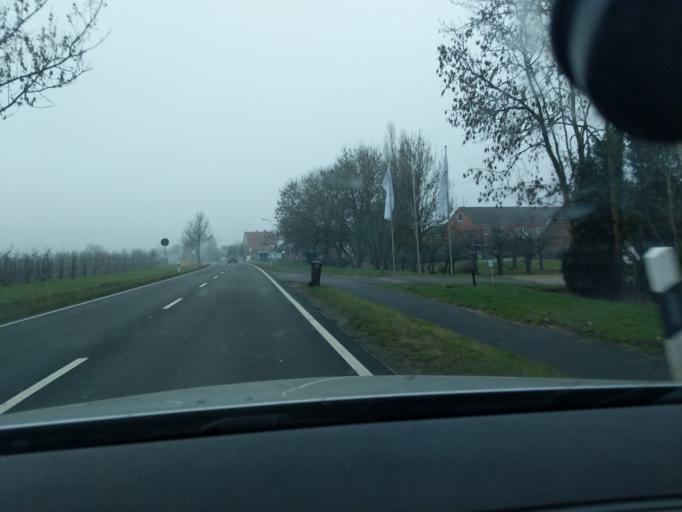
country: DE
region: Lower Saxony
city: Jork
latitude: 53.5437
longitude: 9.6789
